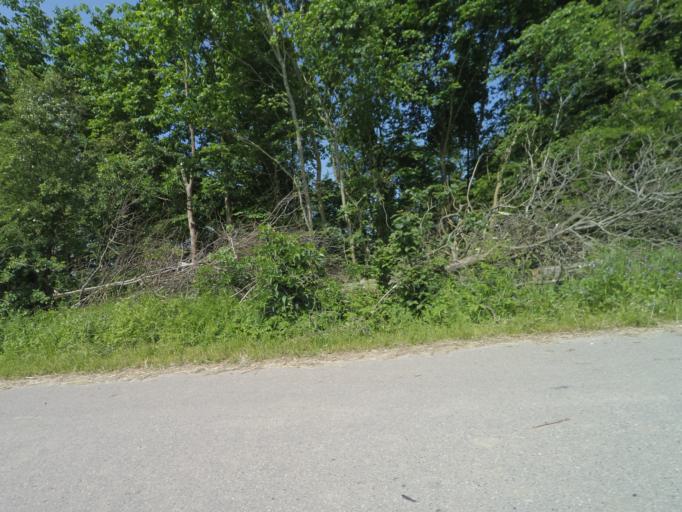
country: DK
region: Central Jutland
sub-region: Arhus Kommune
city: Kolt
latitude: 56.1172
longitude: 10.0508
